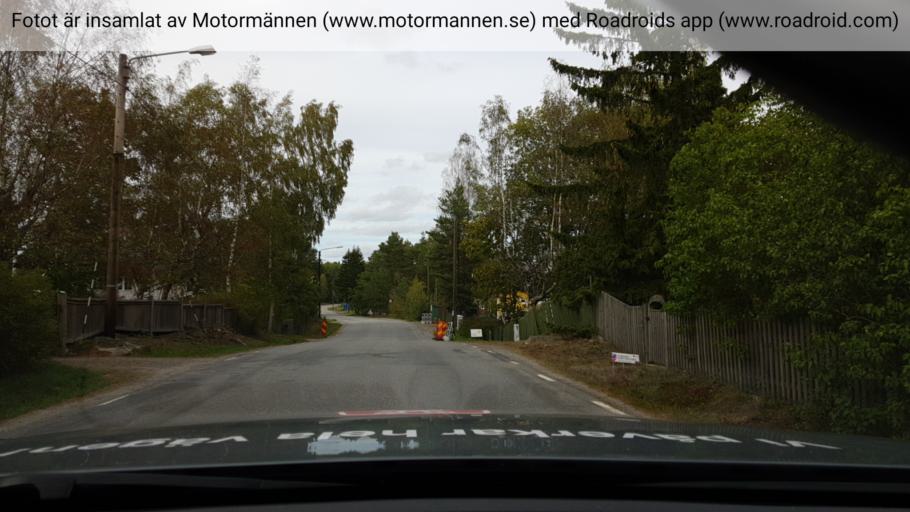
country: SE
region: Stockholm
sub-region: Haninge Kommun
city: Haninge
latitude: 59.0866
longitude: 18.1784
